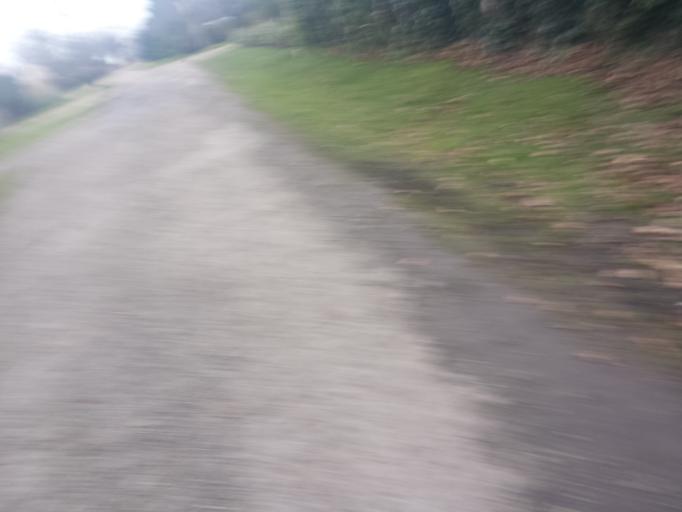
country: GB
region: England
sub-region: Essex
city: Little Clacton
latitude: 51.8617
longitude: 1.1599
